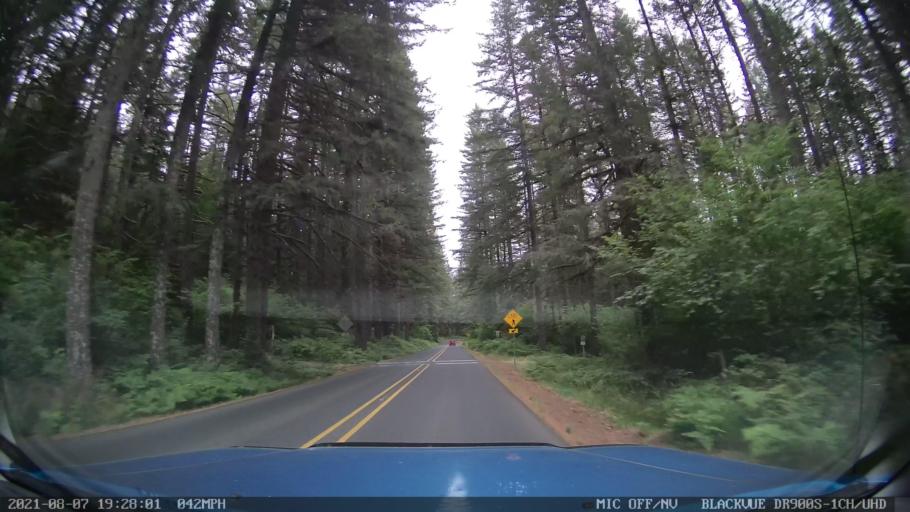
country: US
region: Oregon
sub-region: Linn County
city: Lyons
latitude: 44.8812
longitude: -122.6413
